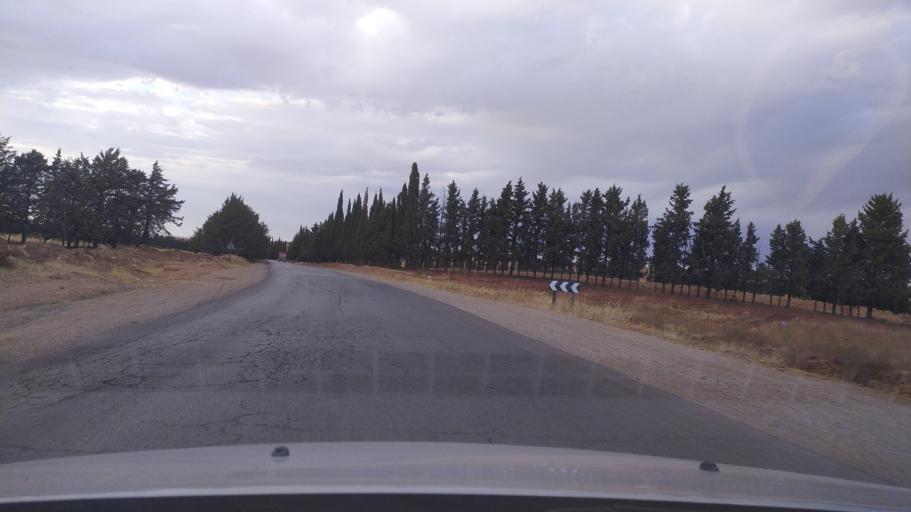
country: DZ
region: Tiaret
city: Frenda
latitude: 35.0429
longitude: 1.0880
